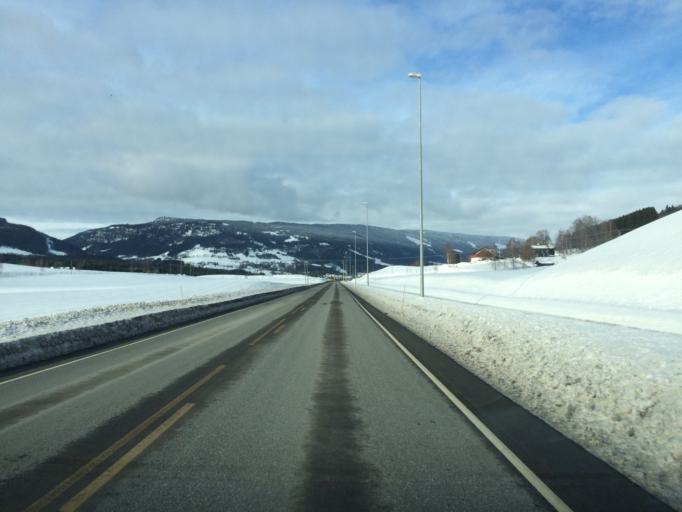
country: NO
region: Oppland
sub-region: Gausdal
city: Segalstad bru
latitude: 61.2203
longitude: 10.2498
